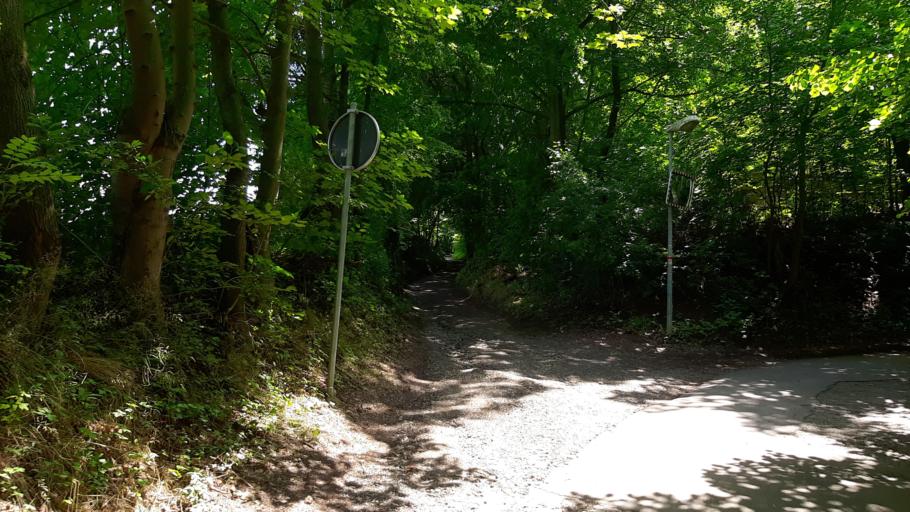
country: DE
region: Thuringia
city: Saalfeld
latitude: 50.6363
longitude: 11.3681
